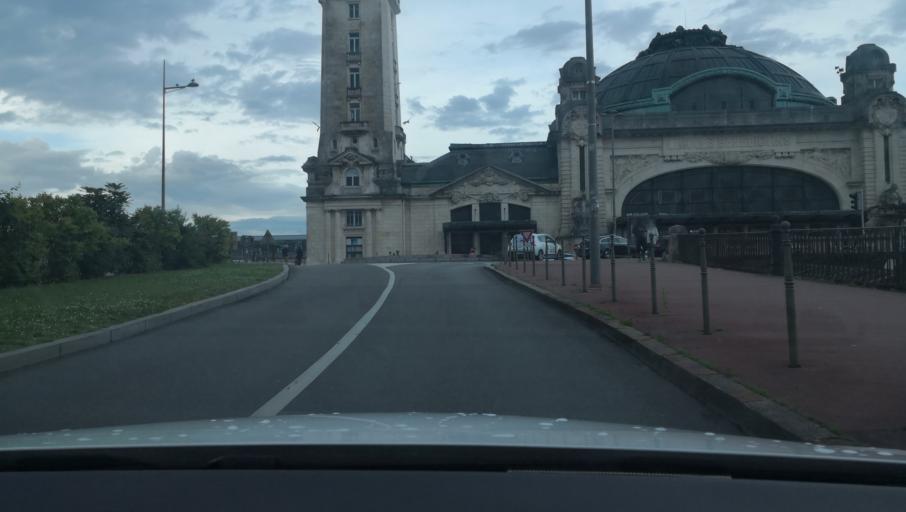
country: FR
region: Limousin
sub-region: Departement de la Haute-Vienne
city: Limoges
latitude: 45.8355
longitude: 1.2666
